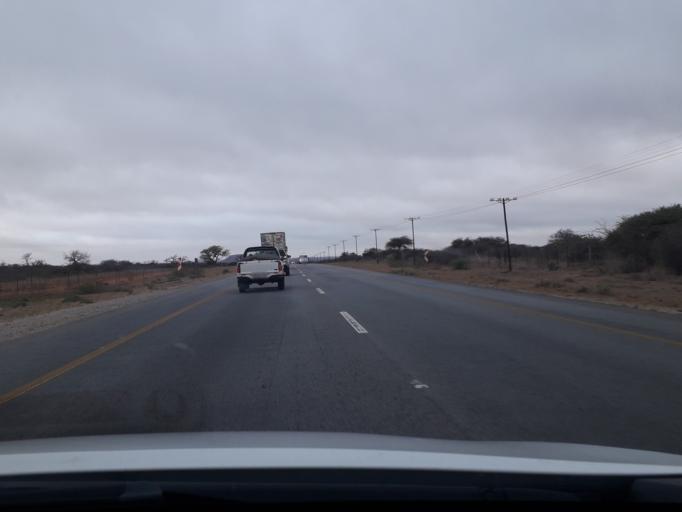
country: ZA
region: Limpopo
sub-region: Capricorn District Municipality
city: Mankoeng
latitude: -23.5776
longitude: 29.6713
